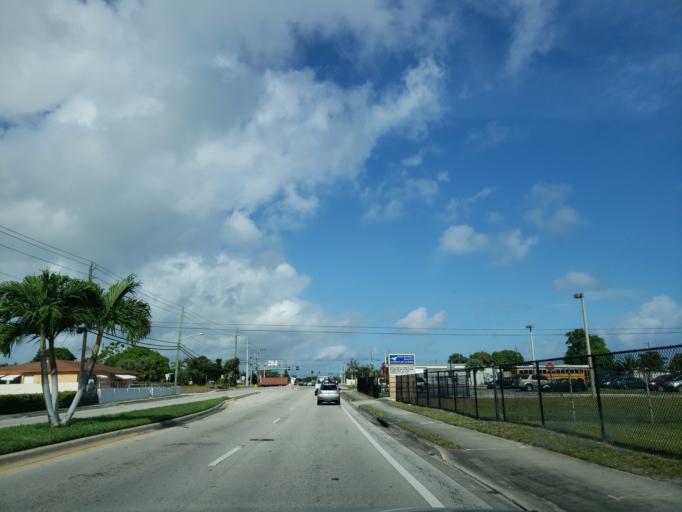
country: US
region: Florida
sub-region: Palm Beach County
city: Mangonia Park
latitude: 26.7673
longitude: -80.0714
